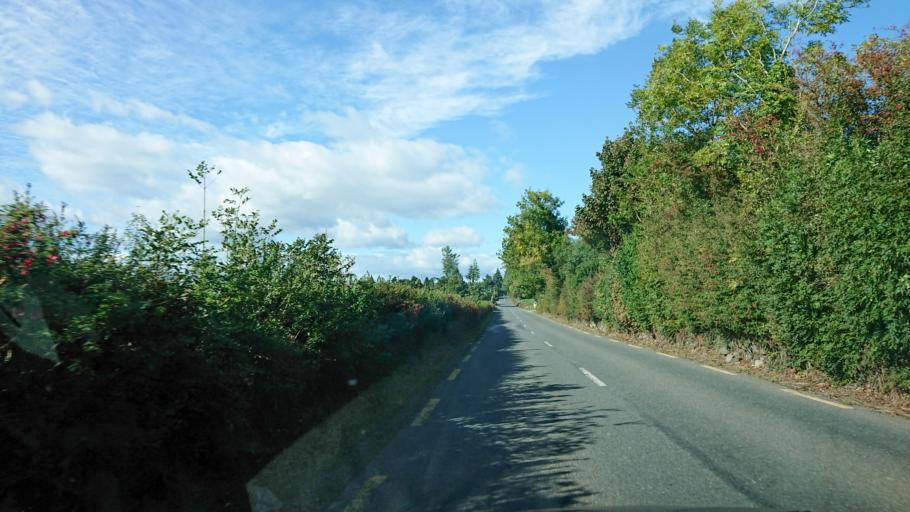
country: IE
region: Munster
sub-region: Waterford
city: Dungarvan
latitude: 52.1907
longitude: -7.6974
